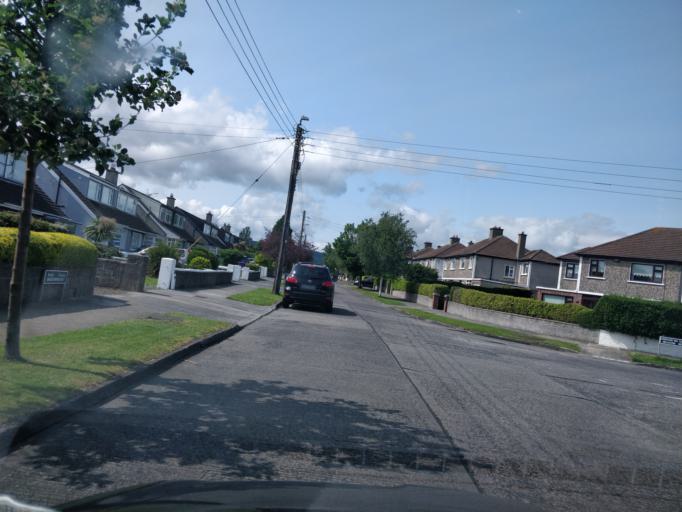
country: IE
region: Leinster
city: Dundrum
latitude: 53.2854
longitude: -6.2601
